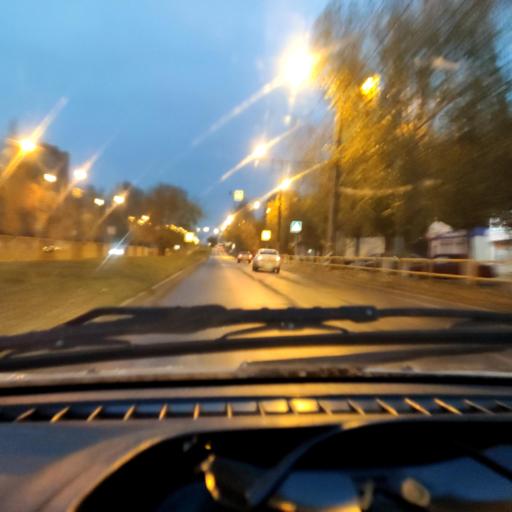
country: RU
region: Samara
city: Zhigulevsk
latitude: 53.4835
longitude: 49.4742
